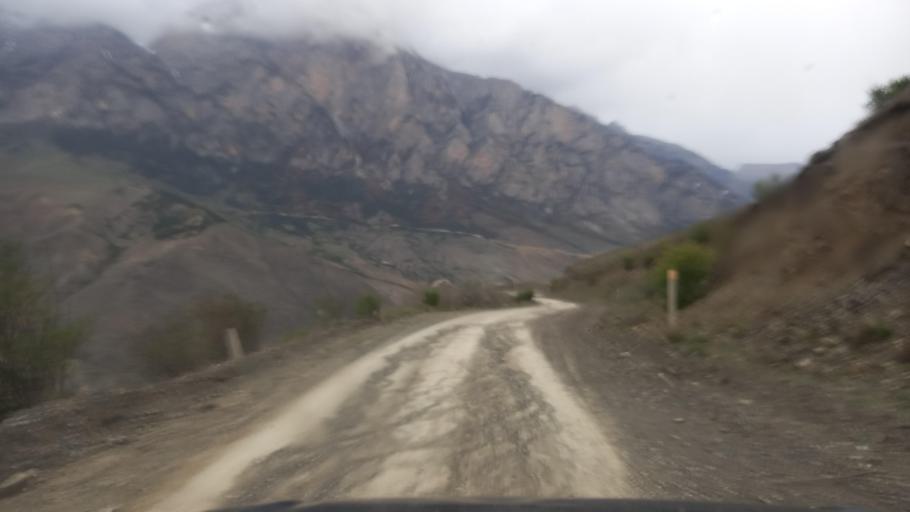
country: RU
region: North Ossetia
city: Mizur
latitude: 42.8585
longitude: 44.1586
